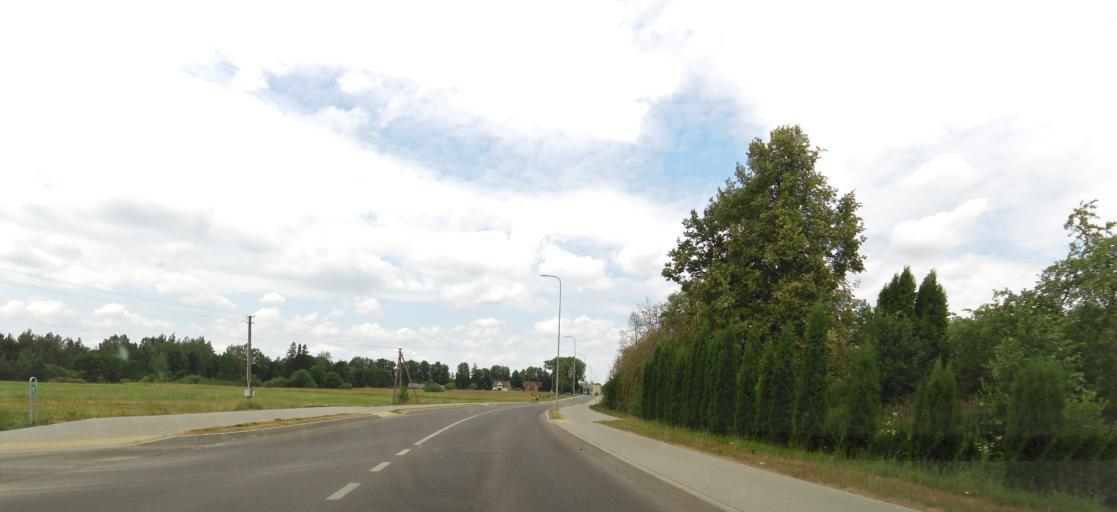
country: LT
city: Sirvintos
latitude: 55.0422
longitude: 24.9675
